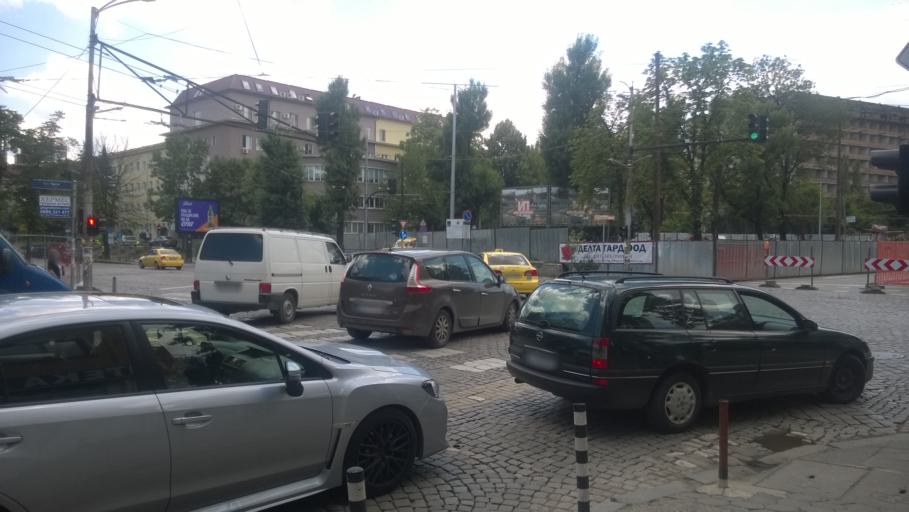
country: BG
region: Sofia-Capital
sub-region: Stolichna Obshtina
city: Sofia
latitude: 42.6873
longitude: 23.3105
